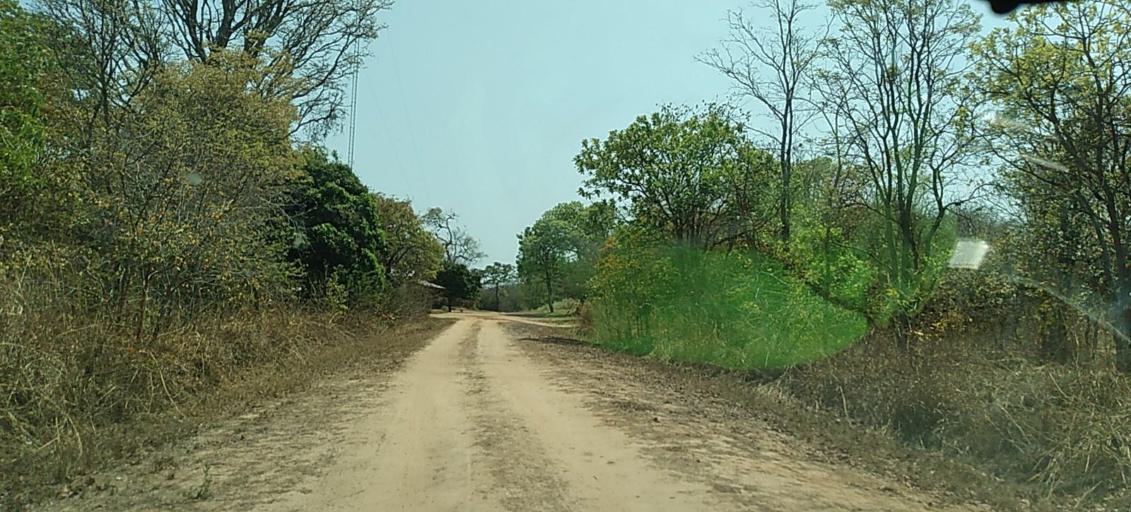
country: ZM
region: North-Western
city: Kalengwa
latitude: -13.1032
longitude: 24.6918
